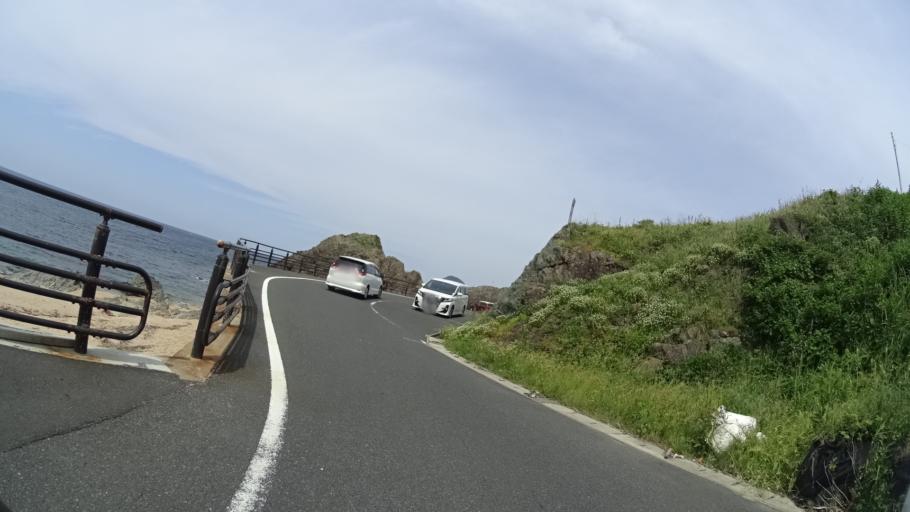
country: JP
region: Kyoto
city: Miyazu
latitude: 35.7409
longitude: 135.0992
